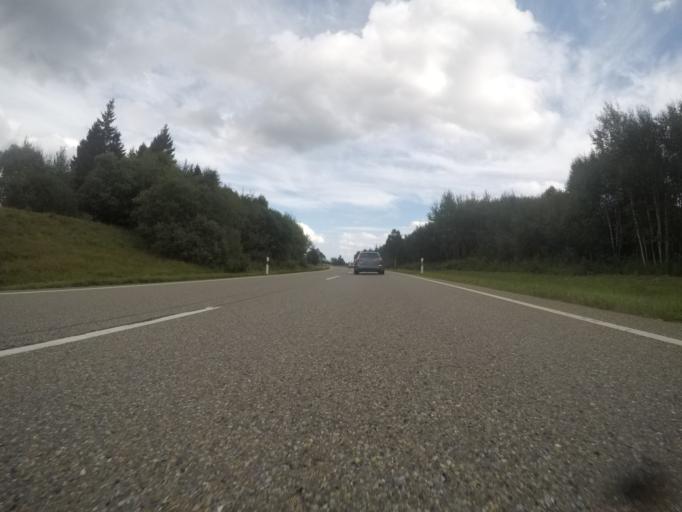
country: DE
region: Baden-Wuerttemberg
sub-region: Freiburg Region
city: Bad Peterstal-Griesbach
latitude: 48.4934
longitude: 8.2622
